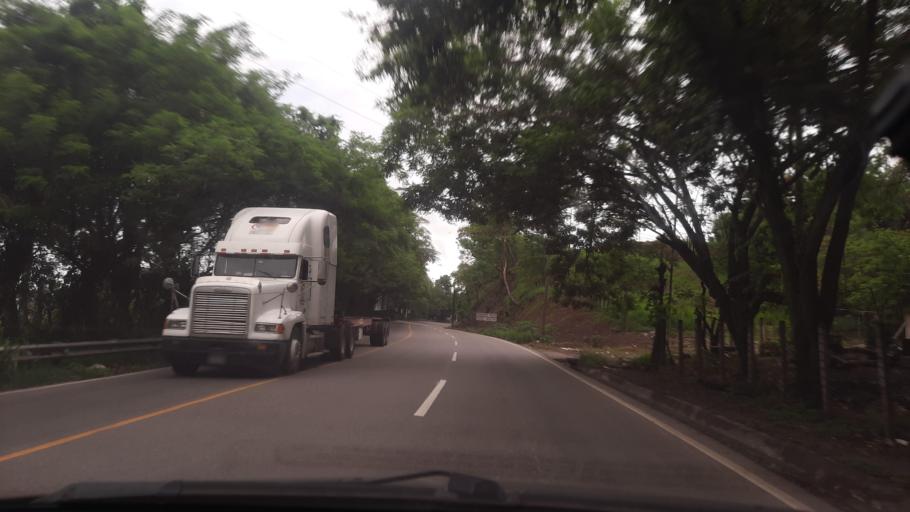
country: GT
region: Izabal
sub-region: Municipio de Los Amates
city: Los Amates
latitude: 15.2530
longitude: -89.1090
